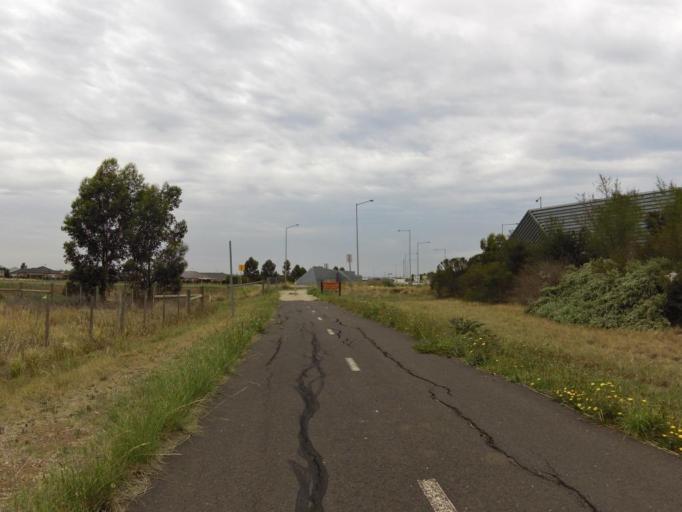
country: AU
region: Victoria
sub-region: Brimbank
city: Derrimut
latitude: -37.7937
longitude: 144.7523
